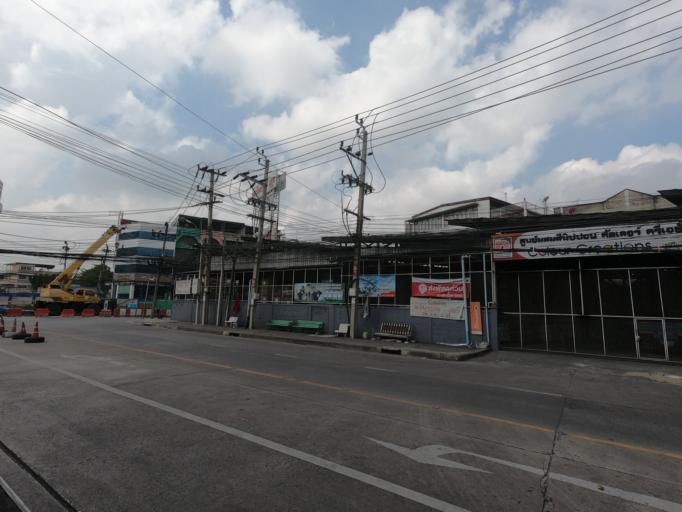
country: TH
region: Bangkok
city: Huai Khwang
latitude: 13.7779
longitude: 100.5873
